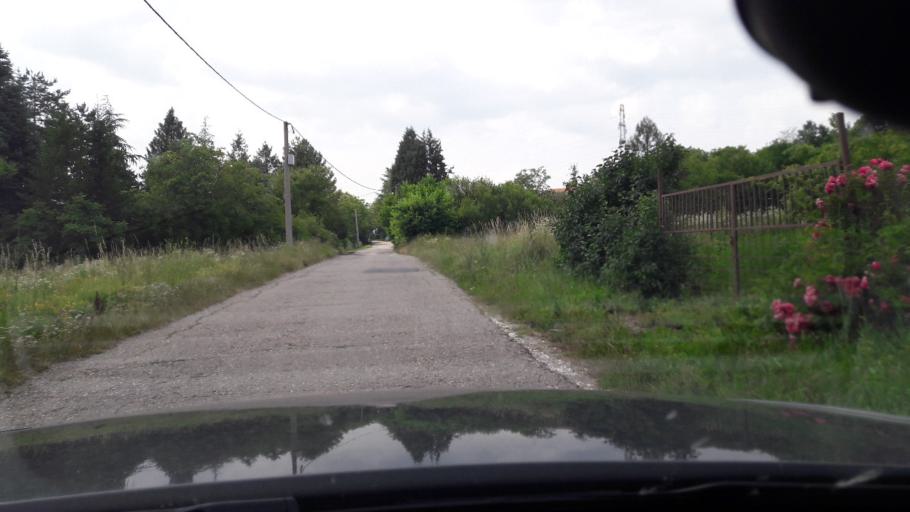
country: RS
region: Central Serbia
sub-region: Belgrade
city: Sopot
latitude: 44.6132
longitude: 20.5919
